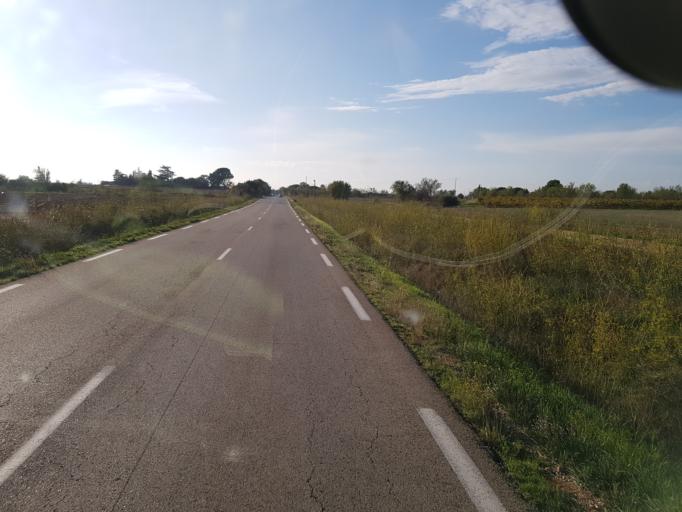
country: FR
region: Languedoc-Roussillon
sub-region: Departement du Gard
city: Redessan
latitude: 43.8272
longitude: 4.5182
